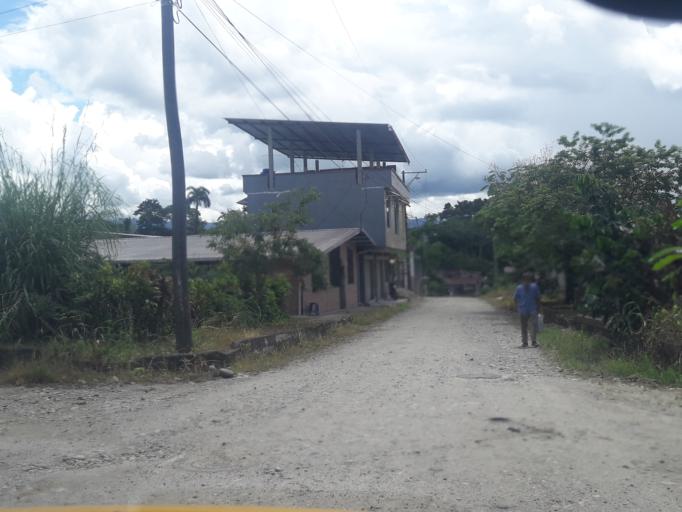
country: EC
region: Napo
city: Tena
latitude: -1.0036
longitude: -77.8182
